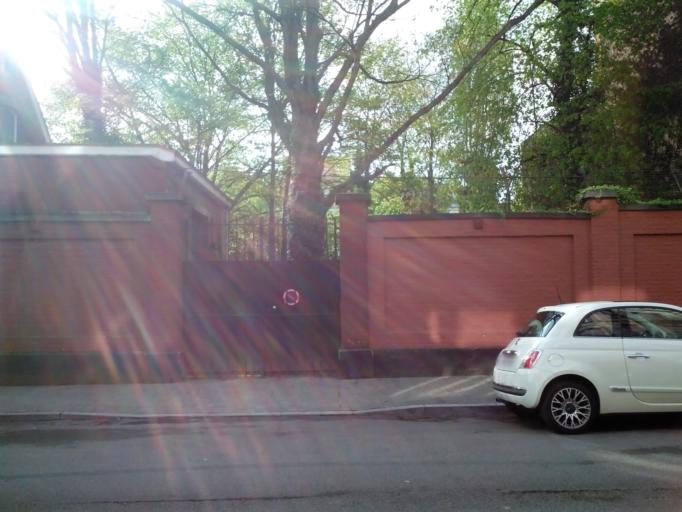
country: BE
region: Brussels Capital
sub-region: Bruxelles-Capitale
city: Brussels
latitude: 50.8481
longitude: 4.3863
